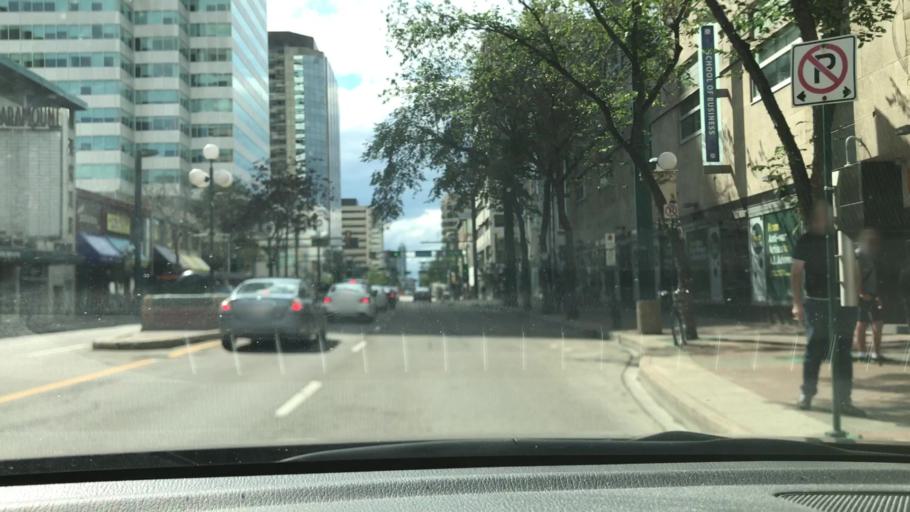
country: CA
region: Alberta
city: Edmonton
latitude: 53.5410
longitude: -113.4958
